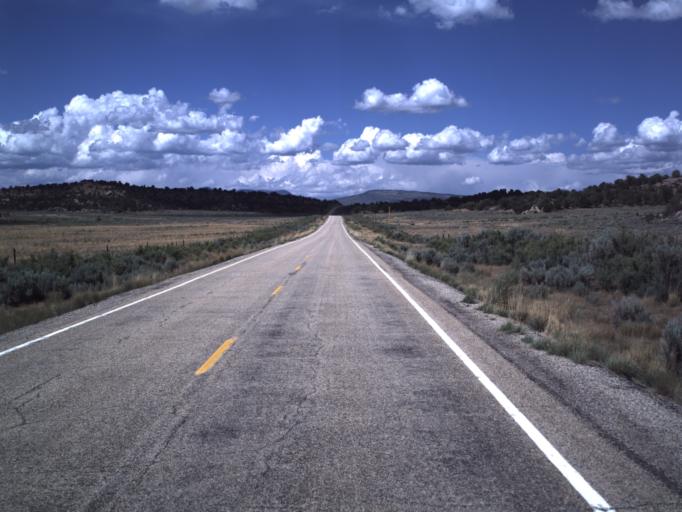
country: US
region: Utah
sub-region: Duchesne County
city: Duchesne
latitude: 40.2302
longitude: -110.7198
